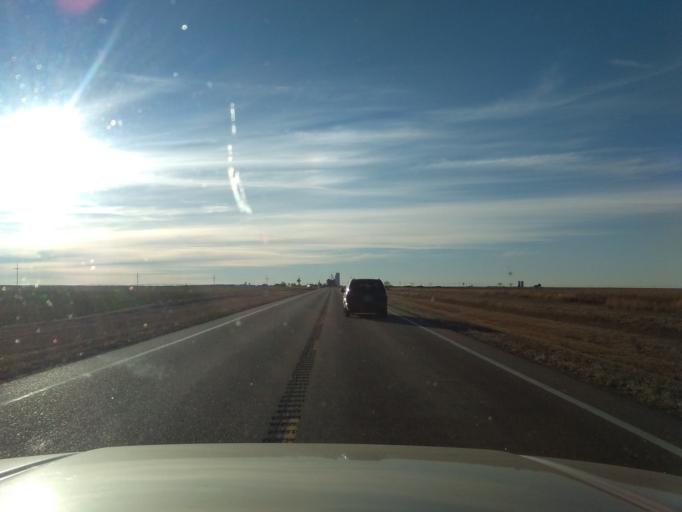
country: US
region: Kansas
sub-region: Thomas County
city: Colby
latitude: 39.4544
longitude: -100.7958
